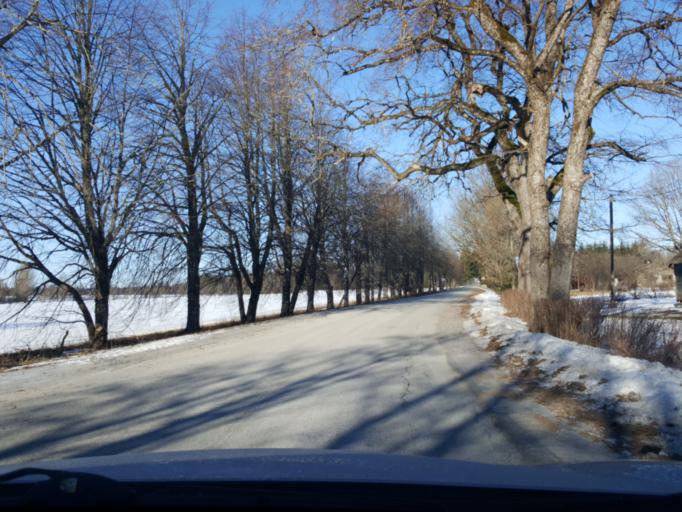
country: EE
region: Viljandimaa
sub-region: Viljandi linn
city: Viljandi
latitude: 58.4234
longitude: 25.5360
